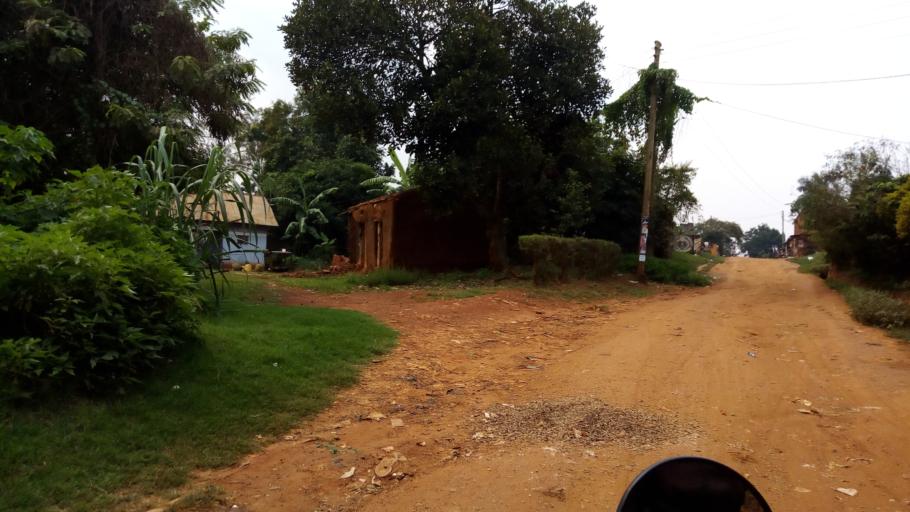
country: UG
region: Central Region
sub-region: Wakiso District
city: Kireka
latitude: 0.3189
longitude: 32.6376
